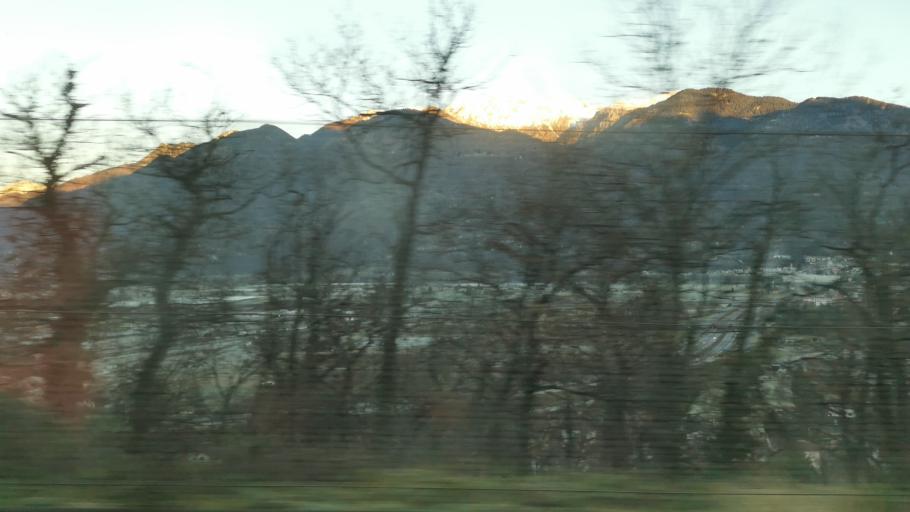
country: CH
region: Ticino
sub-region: Bellinzona District
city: Camorino
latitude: 46.1566
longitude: 8.9928
